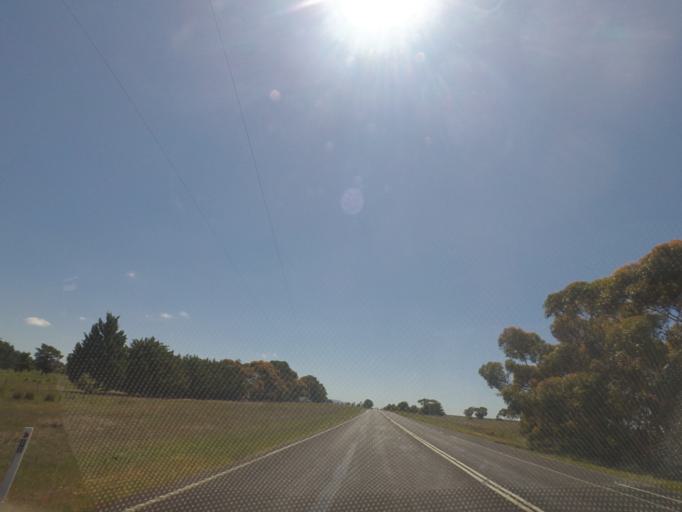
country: AU
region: Victoria
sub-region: Hume
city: Sunbury
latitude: -37.4889
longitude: 144.7556
